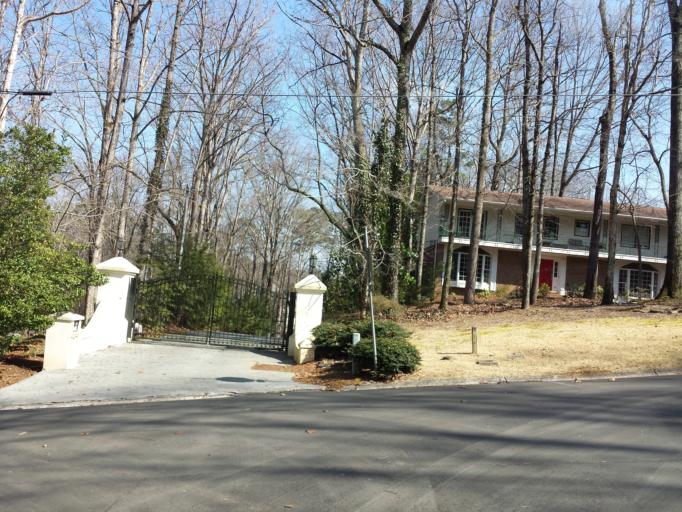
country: US
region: Georgia
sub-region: Cobb County
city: Vinings
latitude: 33.9195
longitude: -84.4582
